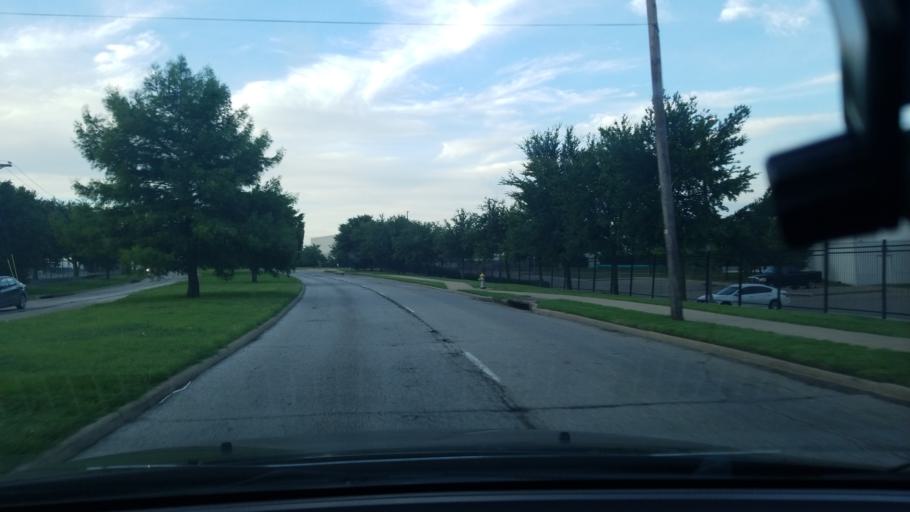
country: US
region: Texas
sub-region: Dallas County
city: Mesquite
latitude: 32.7837
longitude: -96.6682
